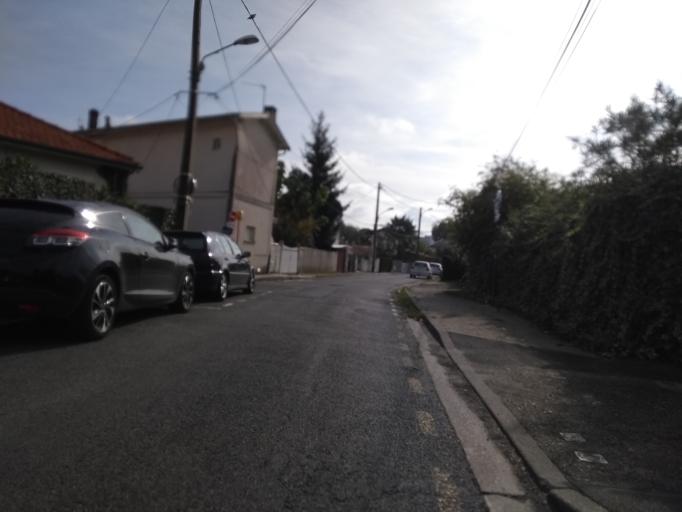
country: FR
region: Aquitaine
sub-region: Departement de la Gironde
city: Pessac
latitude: 44.7993
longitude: -0.6331
